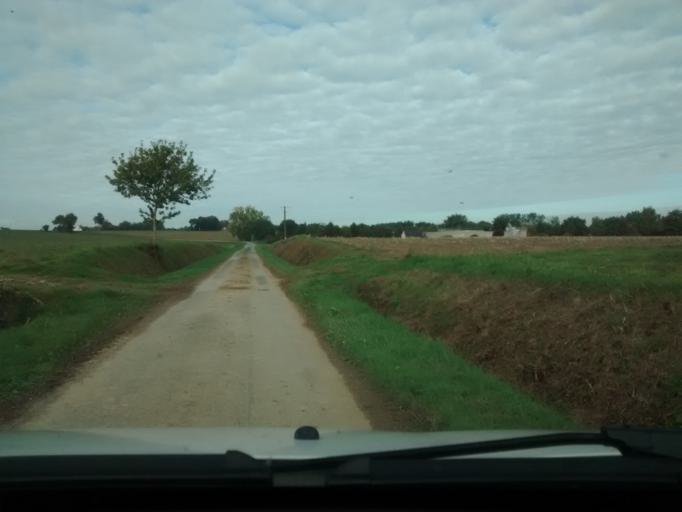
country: FR
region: Brittany
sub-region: Departement d'Ille-et-Vilaine
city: Chavagne
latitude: 48.0786
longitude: -1.7616
